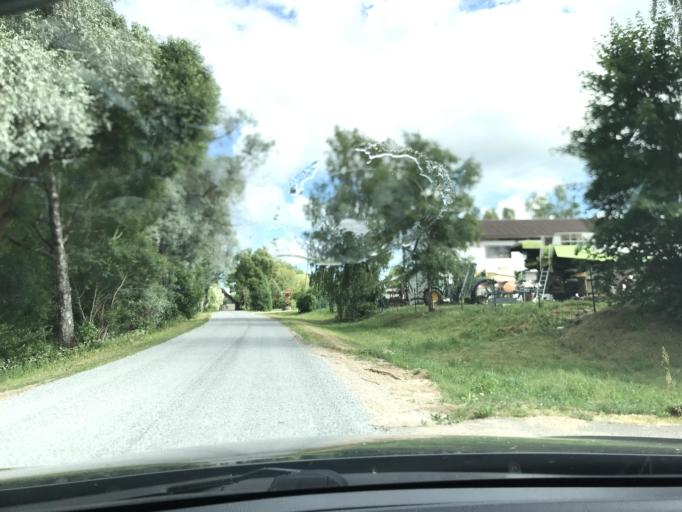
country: LV
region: Alsunga
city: Alsunga
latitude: 56.9827
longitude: 21.6327
